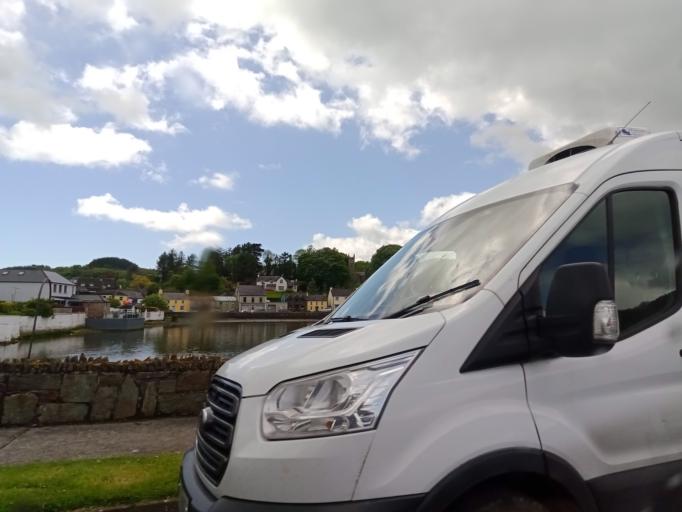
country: IE
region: Munster
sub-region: County Cork
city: Derry
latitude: 51.5595
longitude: -9.1406
